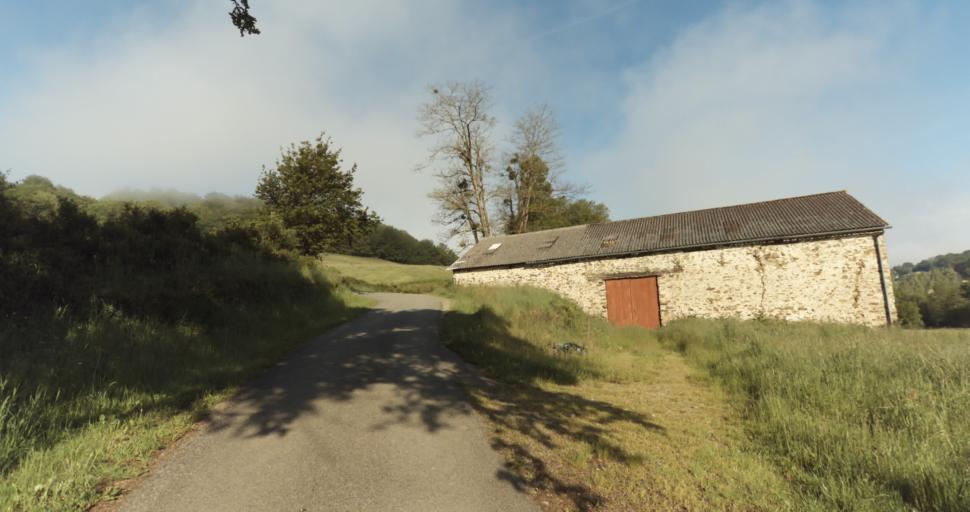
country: FR
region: Limousin
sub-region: Departement de la Haute-Vienne
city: Le Vigen
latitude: 45.7503
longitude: 1.2830
